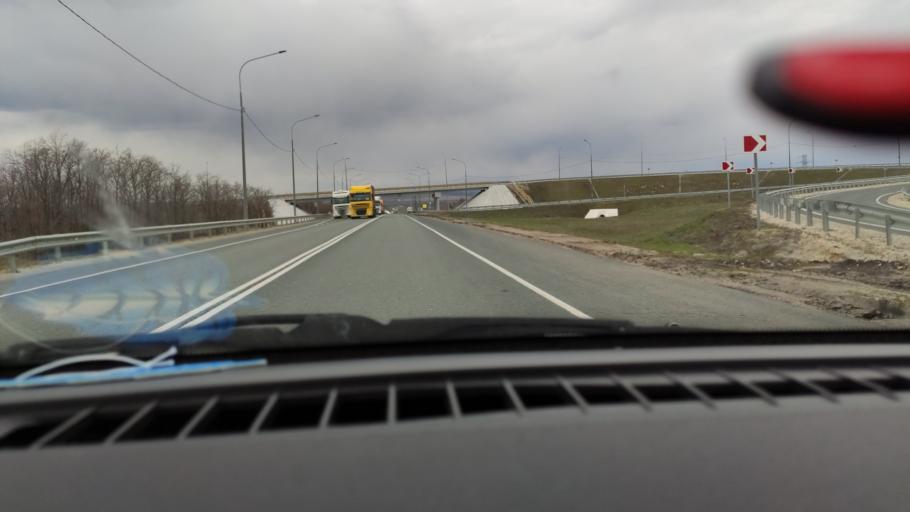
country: RU
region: Saratov
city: Yelshanka
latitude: 51.8256
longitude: 46.2902
